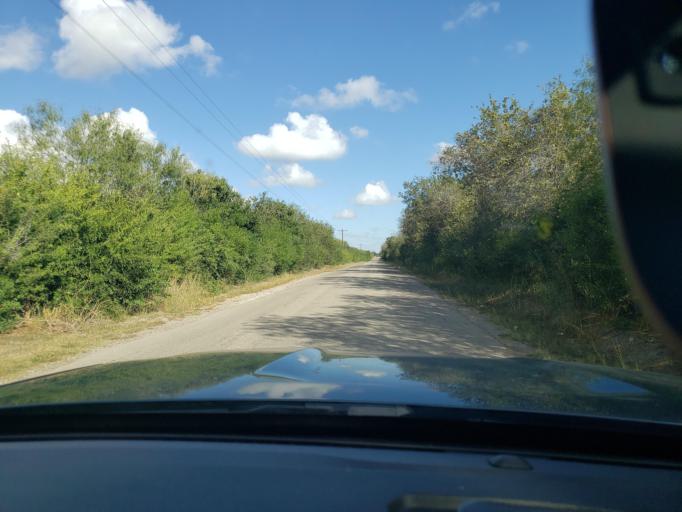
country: US
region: Texas
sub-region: Bee County
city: Beeville
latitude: 28.4521
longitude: -97.7175
